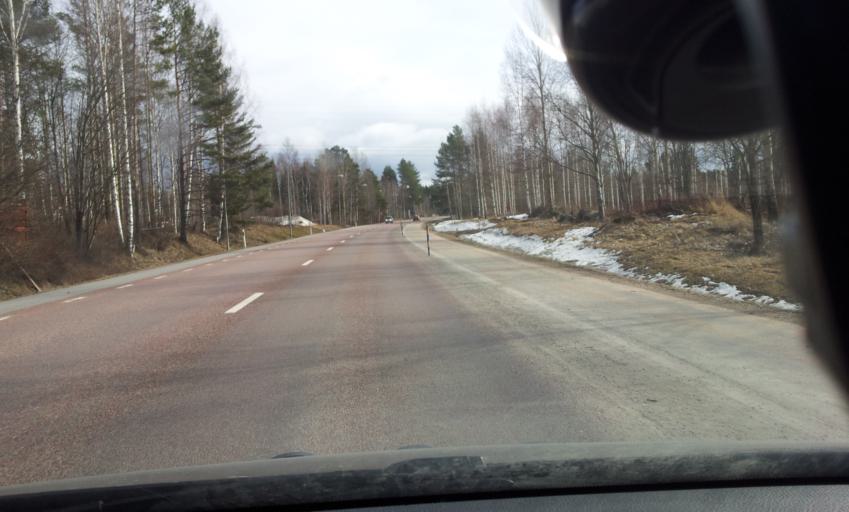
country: SE
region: Gaevleborg
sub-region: Ljusdals Kommun
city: Ljusdal
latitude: 61.8257
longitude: 16.1218
